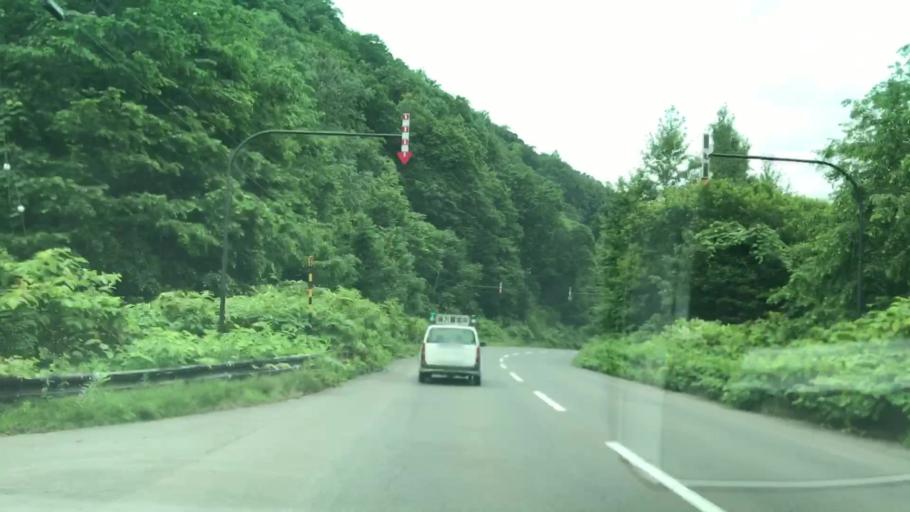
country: JP
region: Hokkaido
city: Yoichi
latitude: 43.0221
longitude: 140.8672
